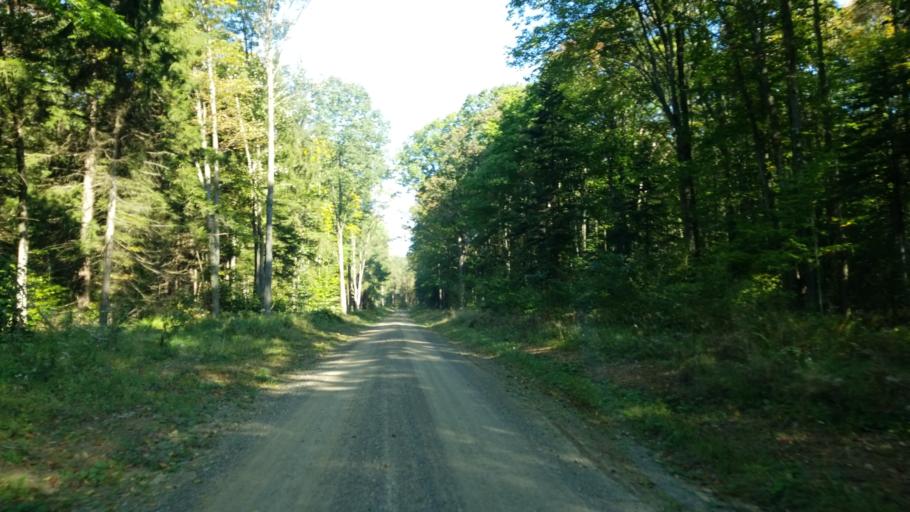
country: US
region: Pennsylvania
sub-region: Clearfield County
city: Treasure Lake
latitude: 41.1282
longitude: -78.5649
